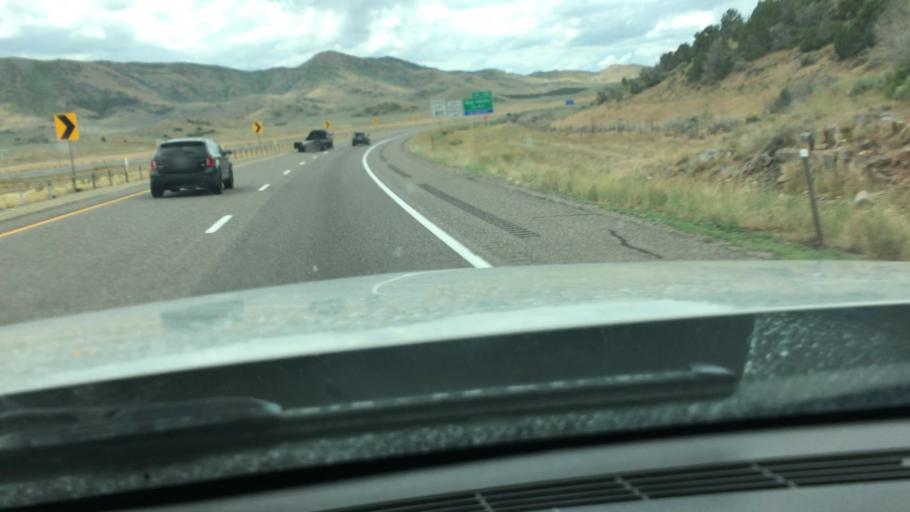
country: US
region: Utah
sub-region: Beaver County
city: Beaver
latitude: 38.6697
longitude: -112.5900
